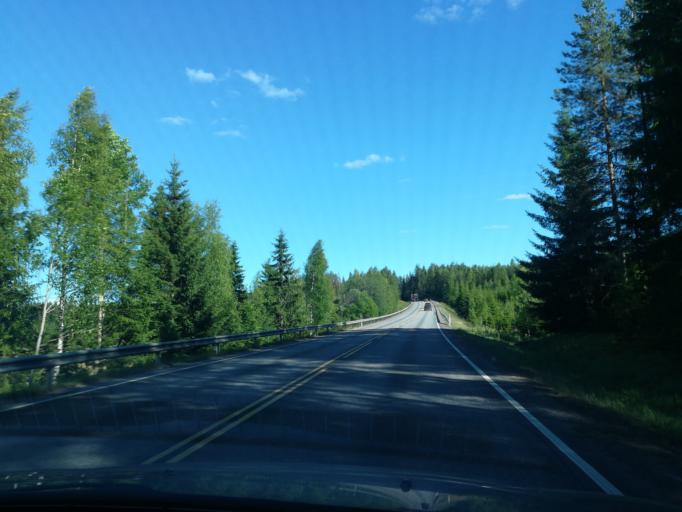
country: FI
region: South Karelia
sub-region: Imatra
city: Ruokolahti
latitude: 61.3623
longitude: 28.6999
